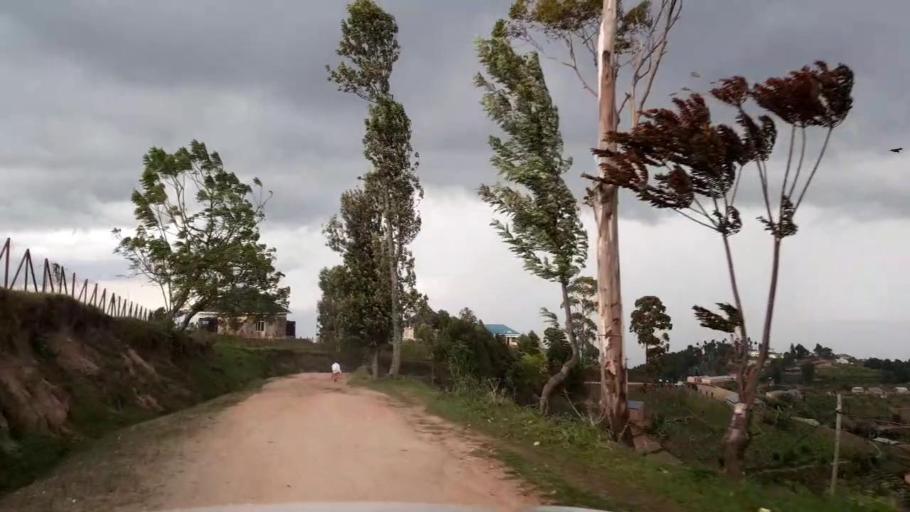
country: RW
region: Southern Province
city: Gitarama
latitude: -1.8728
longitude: 29.5869
